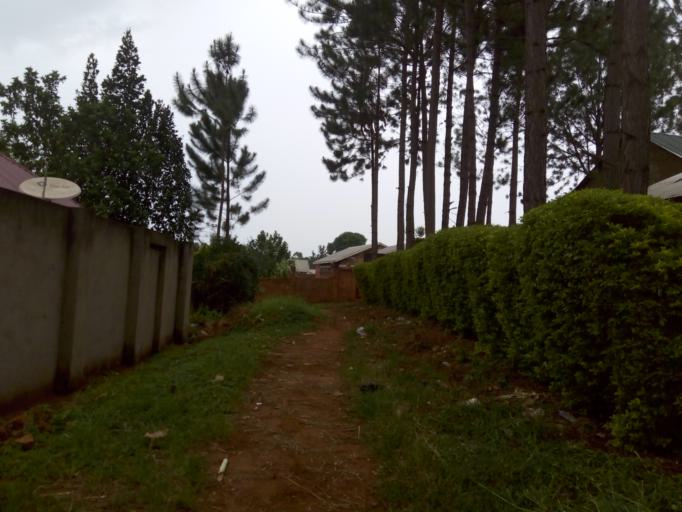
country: UG
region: Western Region
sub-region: Masindi District
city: Masindi
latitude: 1.6823
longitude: 31.7135
